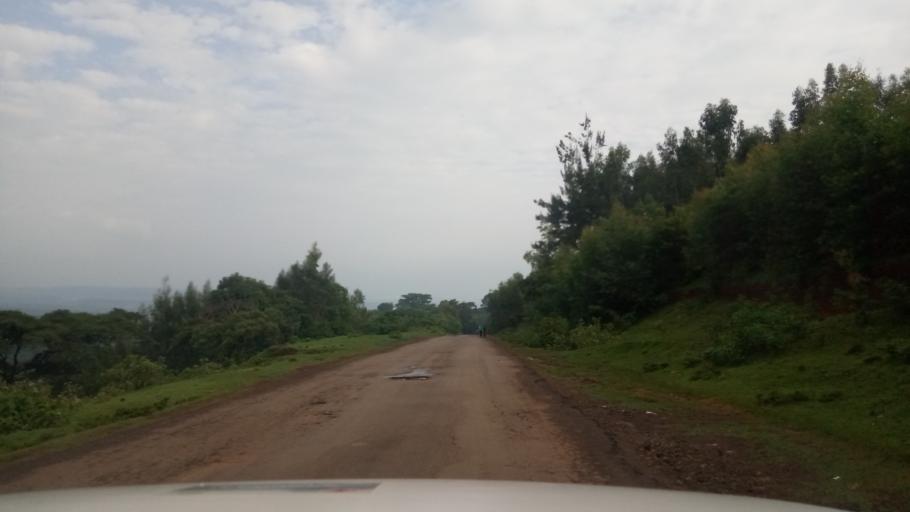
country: ET
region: Oromiya
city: Agaro
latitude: 7.7945
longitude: 36.7232
